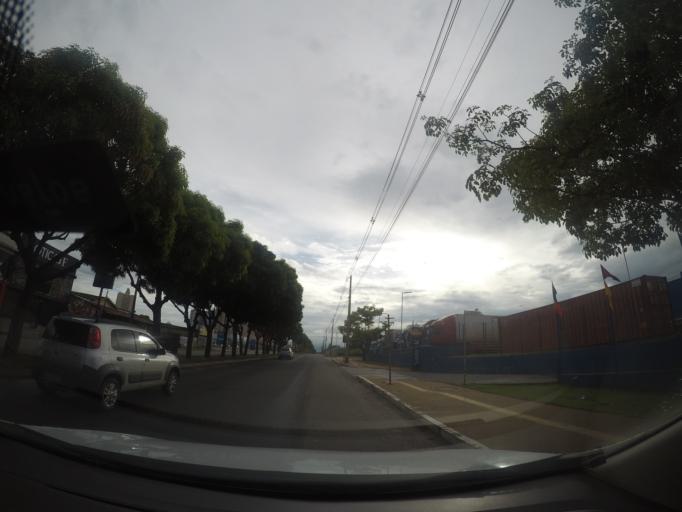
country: BR
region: Goias
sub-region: Goiania
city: Goiania
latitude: -16.7424
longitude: -49.2823
